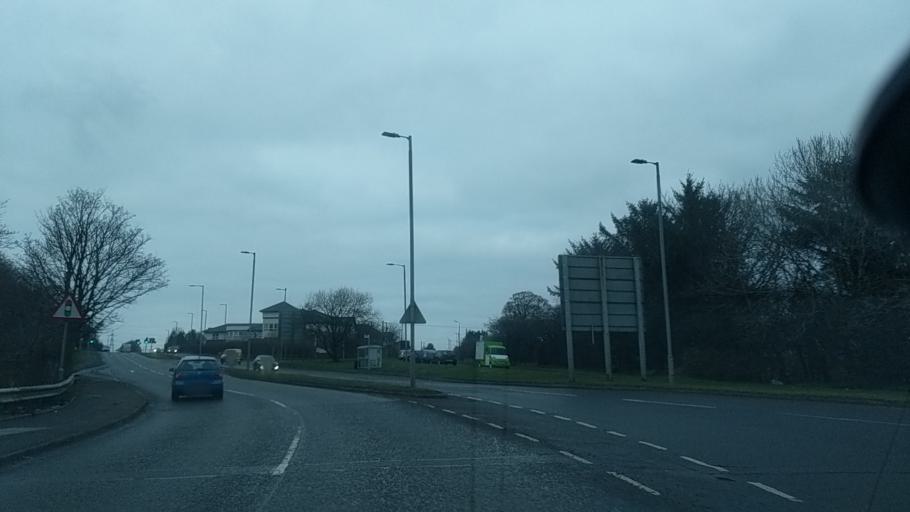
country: GB
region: Scotland
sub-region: South Lanarkshire
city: East Kilbride
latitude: 55.7830
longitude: -4.1655
